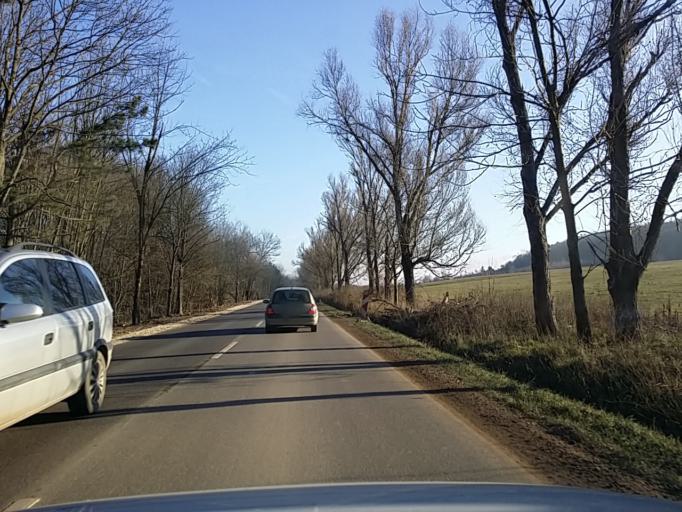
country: HU
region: Pest
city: Solymar
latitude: 47.5689
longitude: 18.9054
